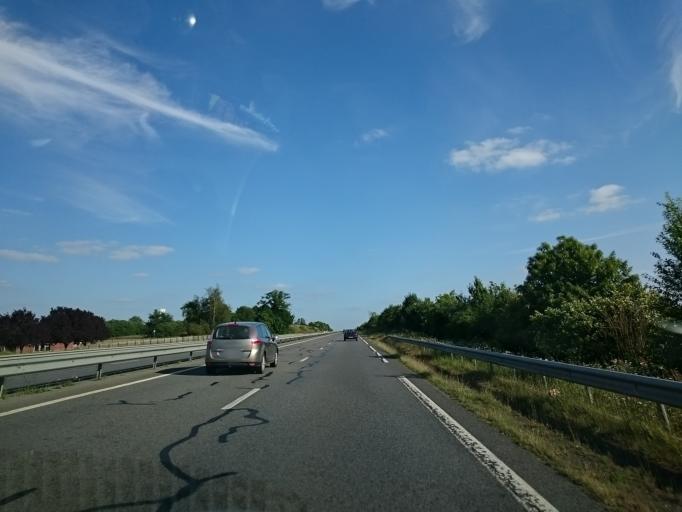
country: FR
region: Brittany
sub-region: Departement d'Ille-et-Vilaine
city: Saint-Armel
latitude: 48.0110
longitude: -1.5996
